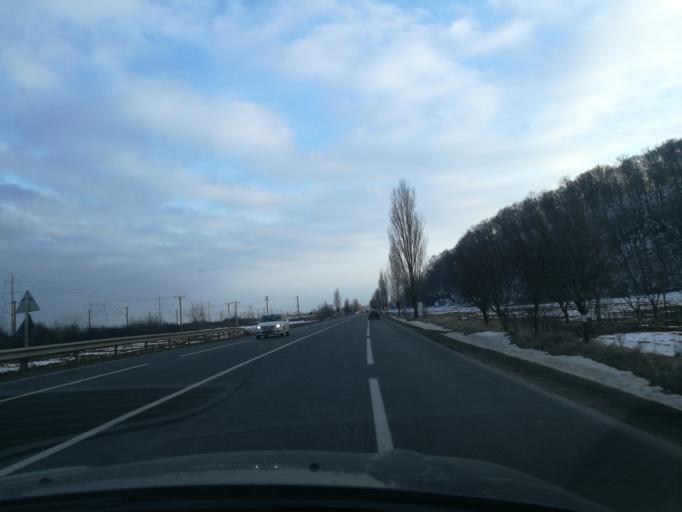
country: RO
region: Bacau
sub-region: Comuna Racaciuni
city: Racaciuni
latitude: 46.3601
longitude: 26.9900
